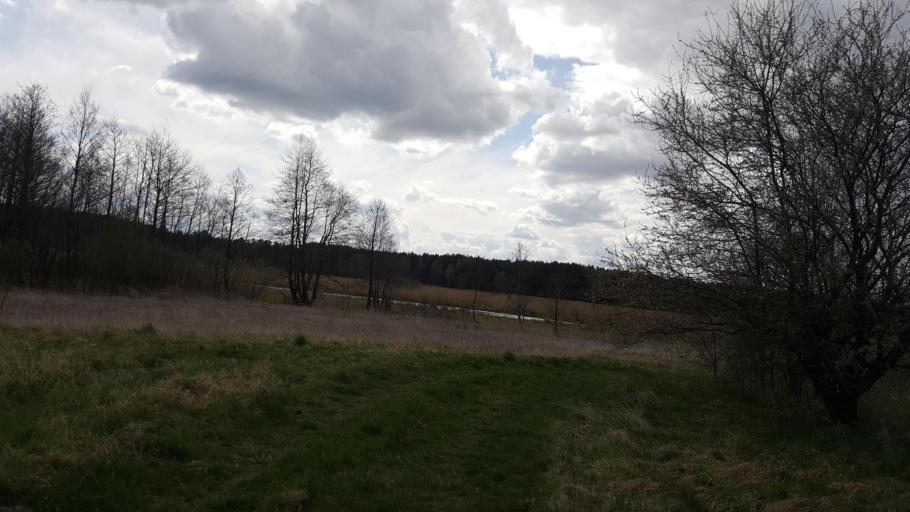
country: BY
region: Brest
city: Kamyanyets
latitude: 52.3495
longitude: 23.7101
